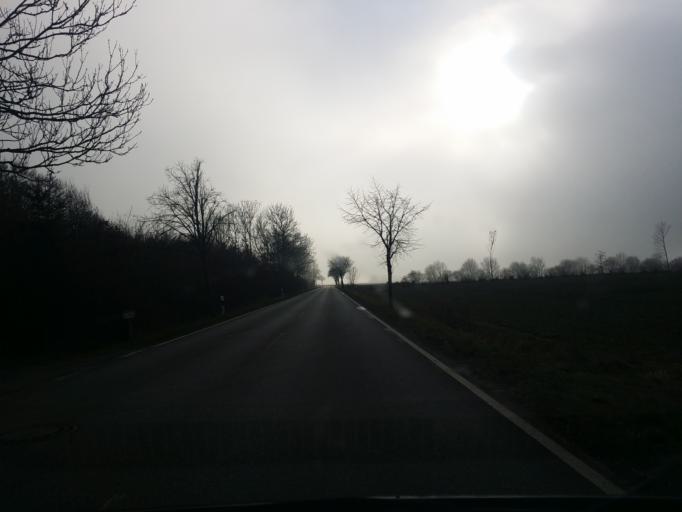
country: DE
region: Schleswig-Holstein
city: Fehmarn
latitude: 54.4459
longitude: 11.1424
